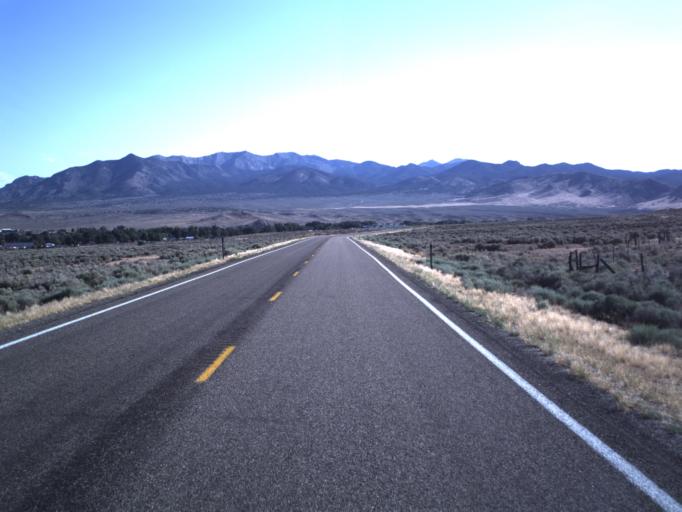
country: US
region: Utah
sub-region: Beaver County
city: Milford
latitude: 38.1966
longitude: -112.9341
